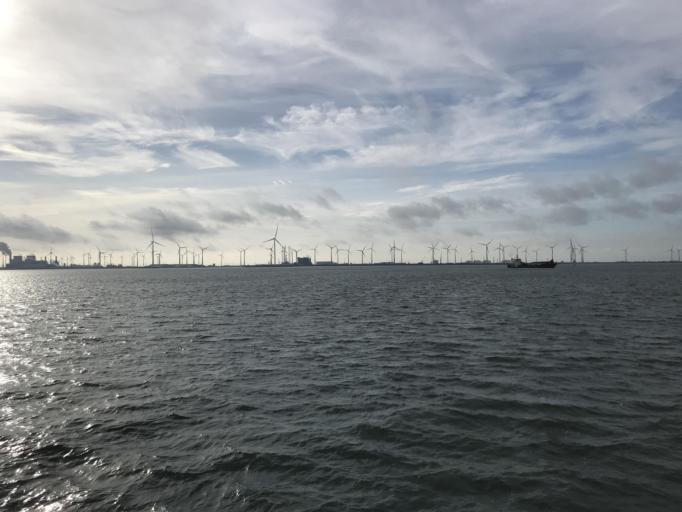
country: NL
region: Groningen
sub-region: Gemeente Appingedam
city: Appingedam
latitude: 53.4867
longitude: 6.8355
